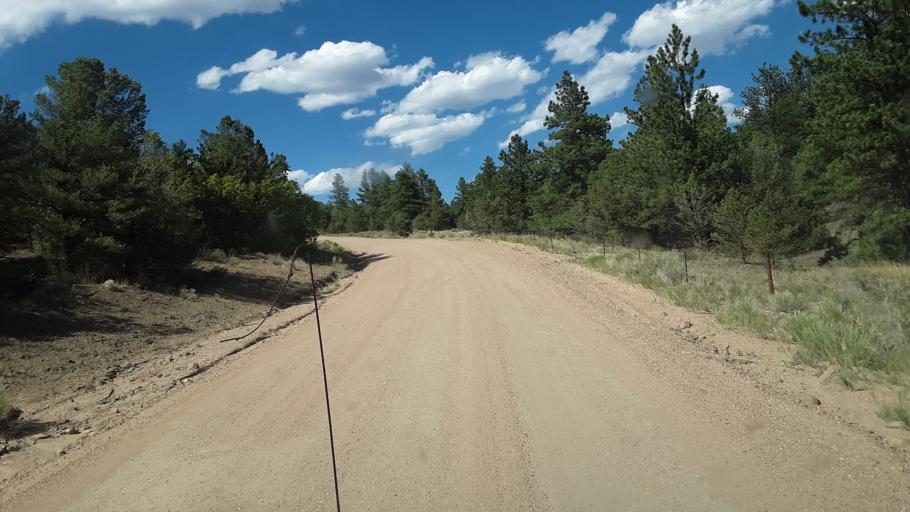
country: US
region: Colorado
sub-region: Custer County
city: Westcliffe
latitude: 38.2536
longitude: -105.5492
